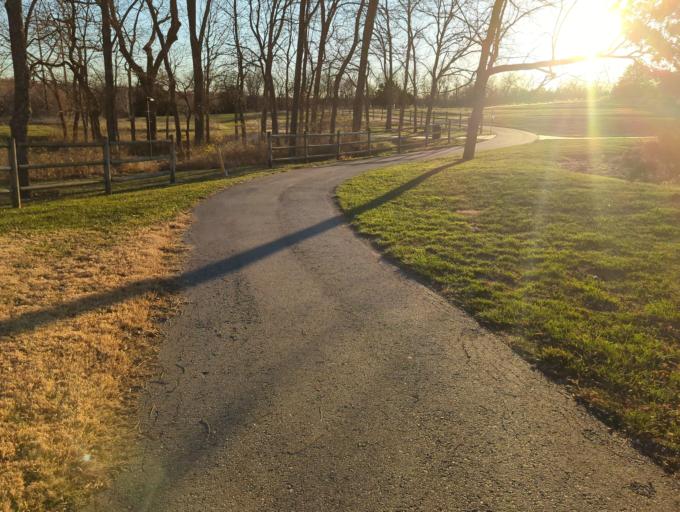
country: US
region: Kansas
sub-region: Johnson County
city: Olathe
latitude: 38.9665
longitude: -94.8413
